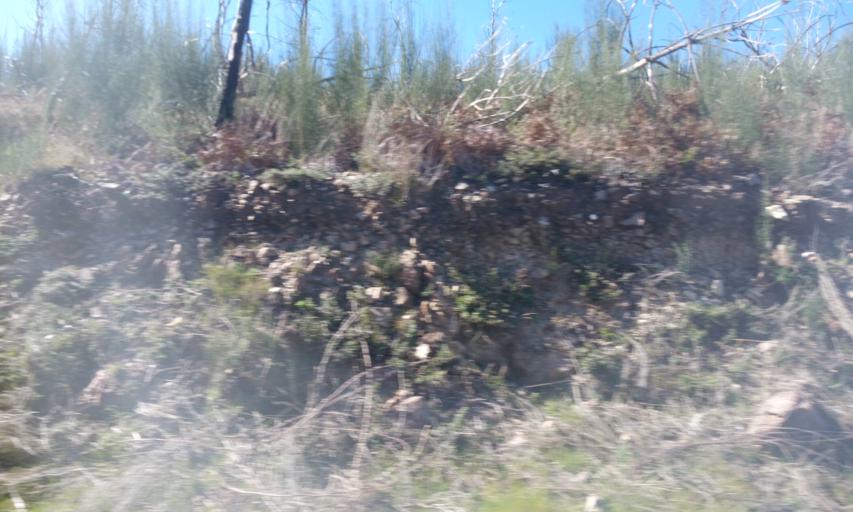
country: PT
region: Guarda
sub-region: Manteigas
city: Manteigas
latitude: 40.4936
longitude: -7.5422
